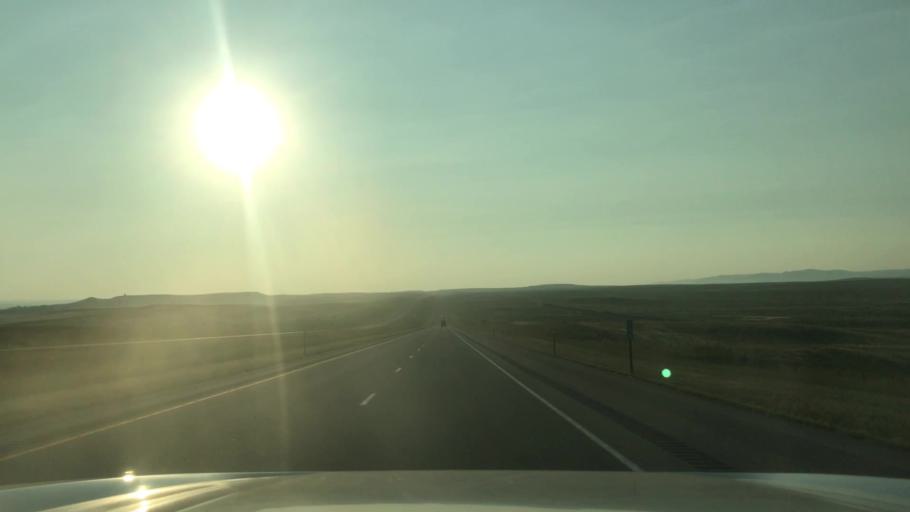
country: US
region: Wyoming
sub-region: Natrona County
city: Evansville
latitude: 42.8399
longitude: -106.1697
